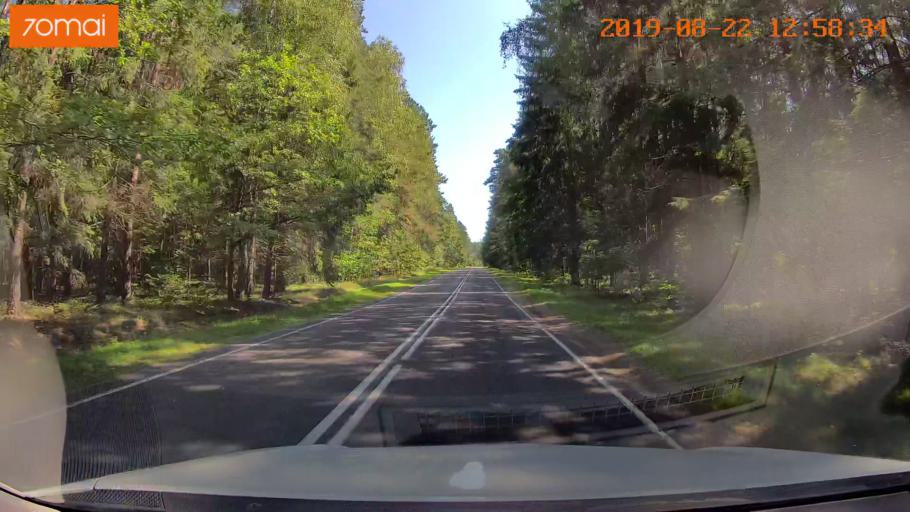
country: BY
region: Minsk
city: Prawdzinski
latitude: 53.4234
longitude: 27.7735
